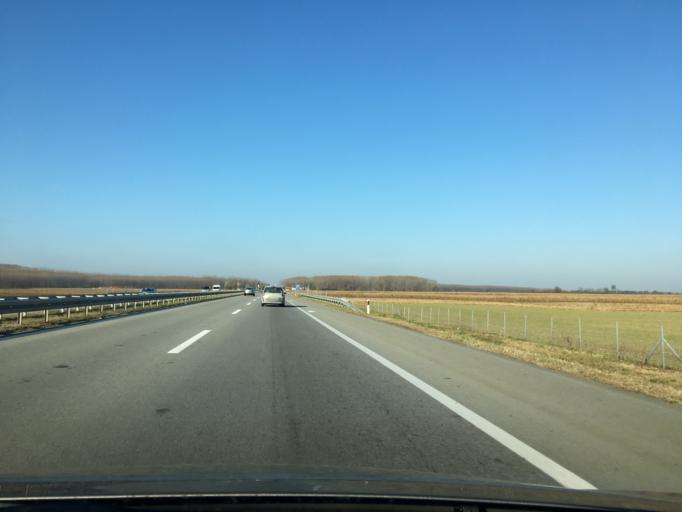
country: RS
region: Autonomna Pokrajina Vojvodina
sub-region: Juznobacki Okrug
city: Petrovaradin
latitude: 45.2728
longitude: 19.9372
